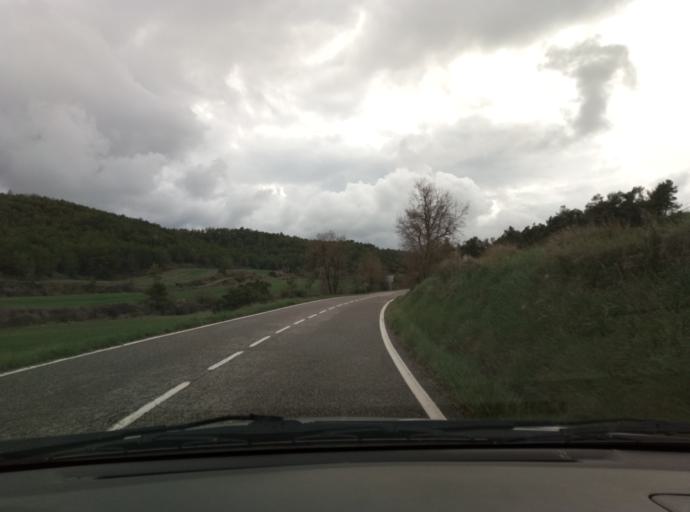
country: ES
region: Catalonia
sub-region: Provincia de Tarragona
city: Santa Coloma de Queralt
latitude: 41.5413
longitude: 1.3453
